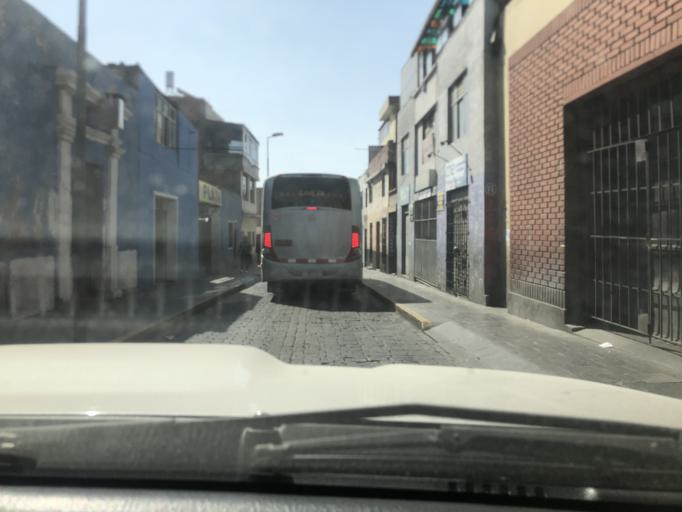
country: PE
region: Arequipa
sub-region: Provincia de Arequipa
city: Arequipa
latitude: -16.3953
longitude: -71.5315
